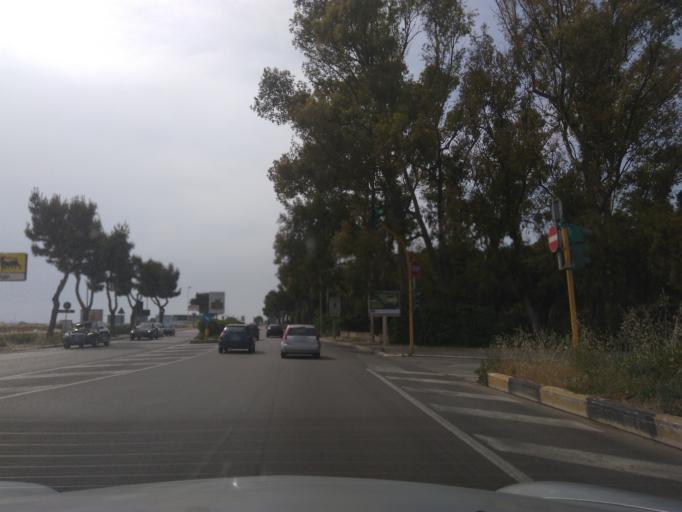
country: IT
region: Apulia
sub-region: Provincia di Bari
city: Bari
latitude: 41.1303
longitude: 16.8313
